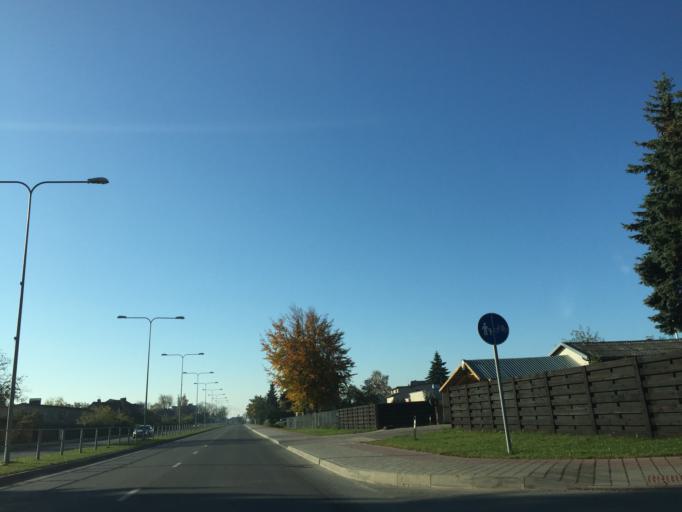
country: LT
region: Klaipedos apskritis
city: Kretinga
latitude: 55.8909
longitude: 21.2340
